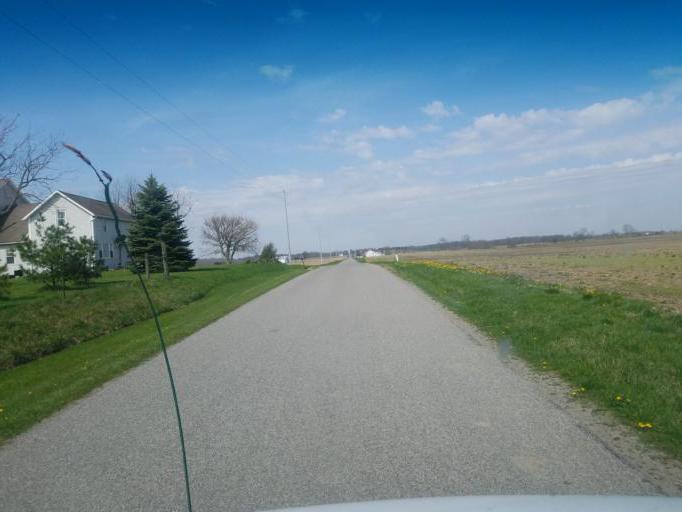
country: US
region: Ohio
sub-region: Logan County
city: Northwood
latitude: 40.4993
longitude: -83.6485
